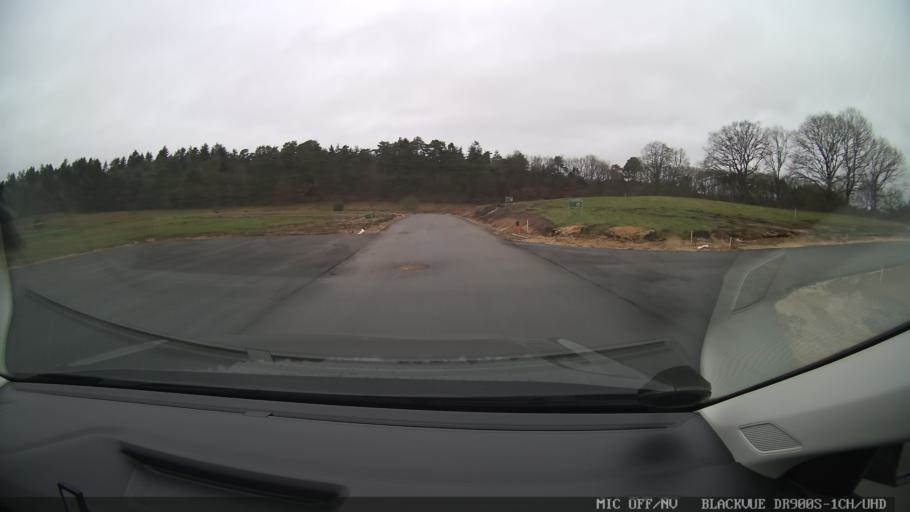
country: DK
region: Central Jutland
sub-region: Viborg Kommune
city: Viborg
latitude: 56.4139
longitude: 9.3725
